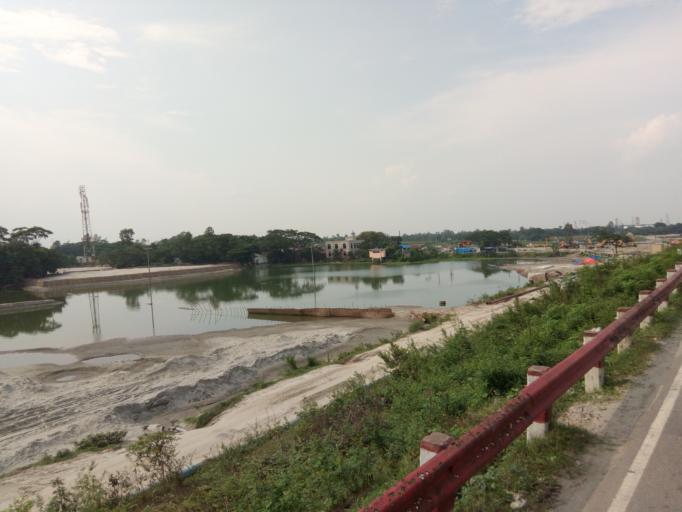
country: BD
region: Dhaka
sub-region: Dhaka
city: Dhaka
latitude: 23.6338
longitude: 90.3452
